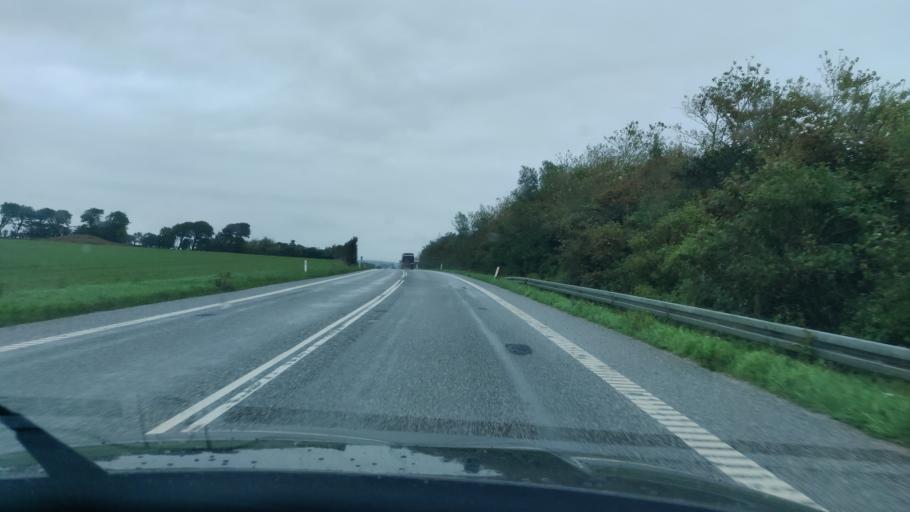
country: DK
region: North Denmark
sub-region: Thisted Kommune
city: Thisted
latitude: 56.9735
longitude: 8.7490
